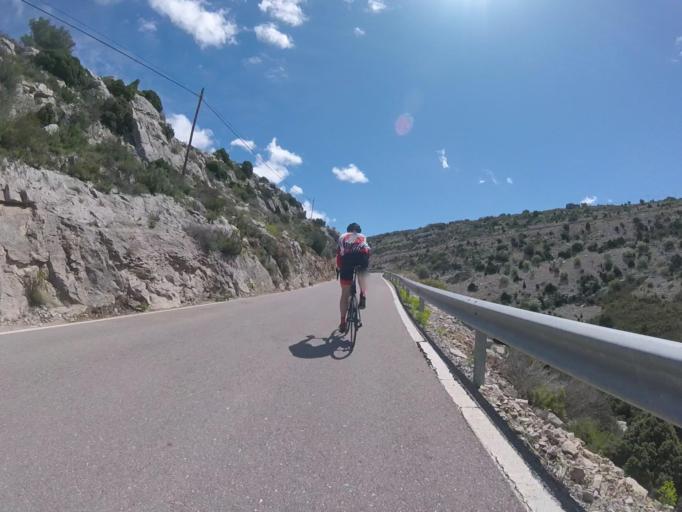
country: ES
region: Valencia
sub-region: Provincia de Castello
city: Sierra-Engarceran
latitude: 40.2788
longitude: -0.0320
